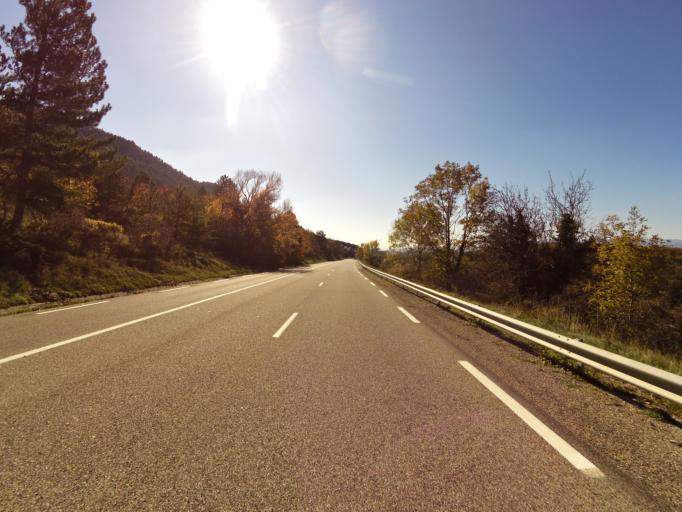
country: FR
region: Rhone-Alpes
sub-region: Departement de l'Ardeche
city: Vesseaux
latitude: 44.6908
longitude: 4.4718
